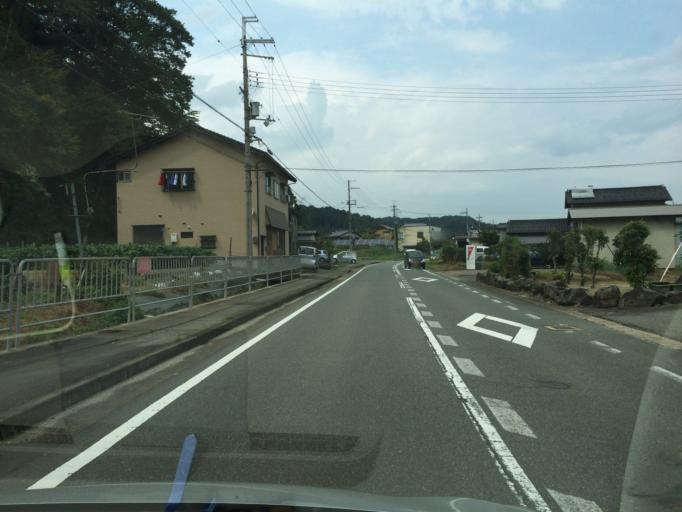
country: JP
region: Hyogo
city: Toyooka
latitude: 35.5237
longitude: 134.8181
